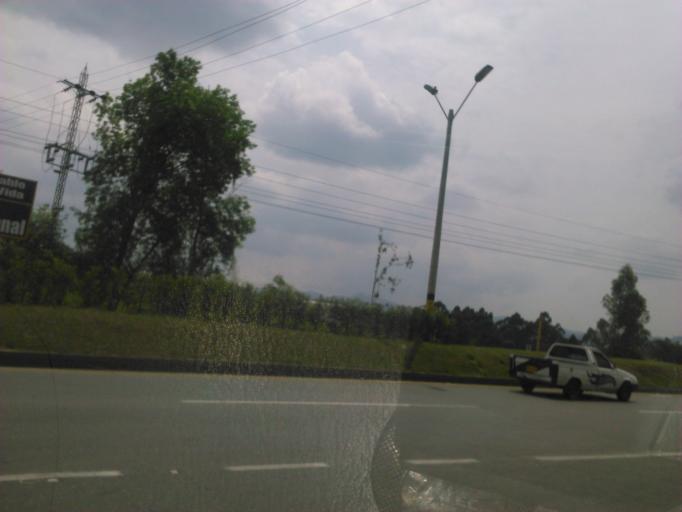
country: CO
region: Antioquia
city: San Vicente
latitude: 6.2252
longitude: -75.3932
